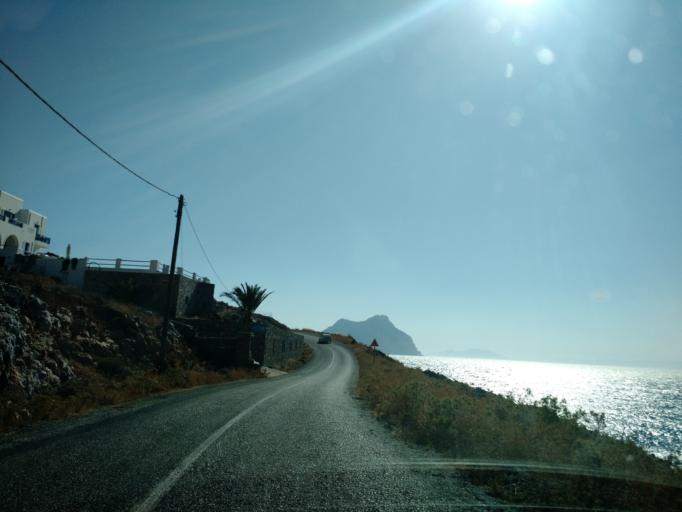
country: GR
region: South Aegean
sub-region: Nomos Kykladon
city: Amorgos
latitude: 36.8948
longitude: 25.9668
